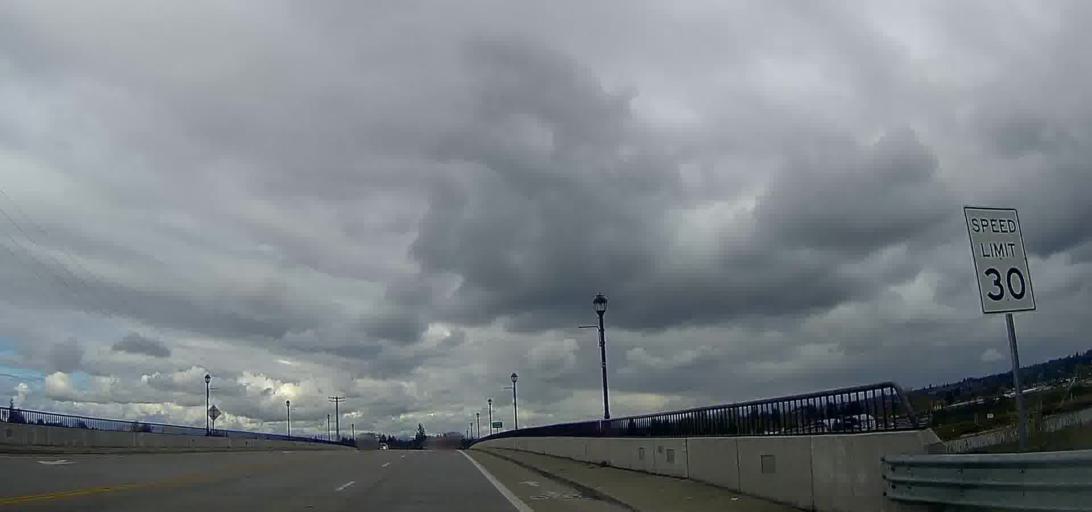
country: US
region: Washington
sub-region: Snohomish County
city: Marysville
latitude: 48.0452
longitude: -122.1788
